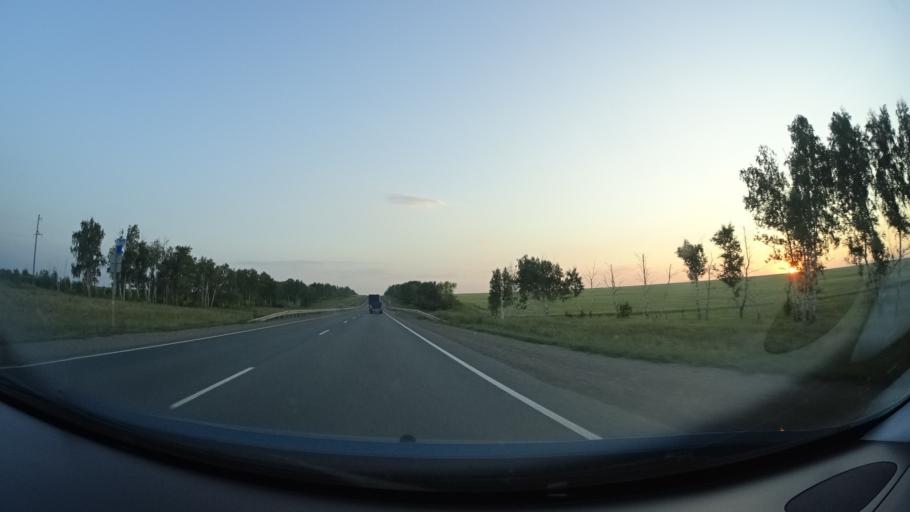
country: RU
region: Samara
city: Sukhodol
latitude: 53.8370
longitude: 51.0995
